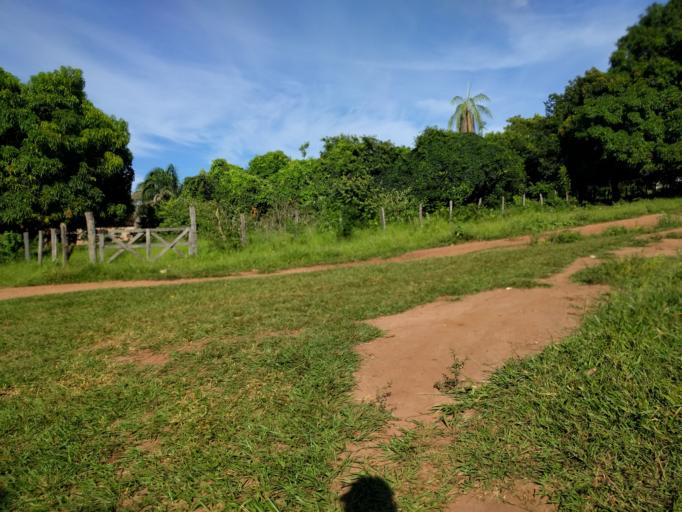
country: BO
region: Santa Cruz
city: Robore
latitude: -18.3349
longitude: -59.5907
